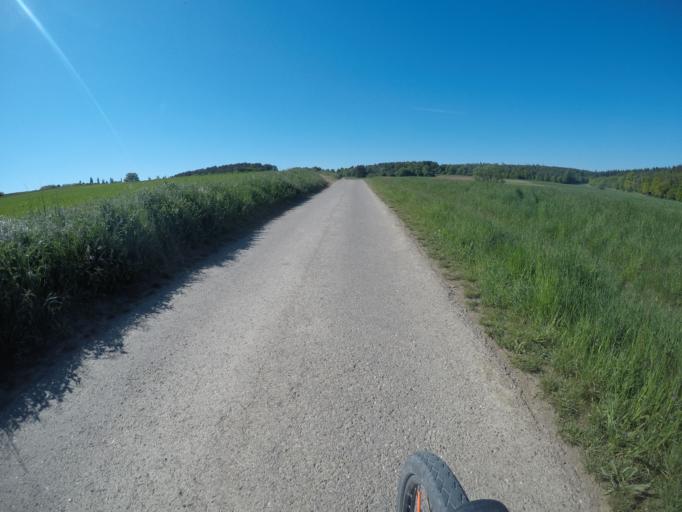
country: DE
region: Baden-Wuerttemberg
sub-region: Karlsruhe Region
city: Heimsheim
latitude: 48.8198
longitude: 8.8548
